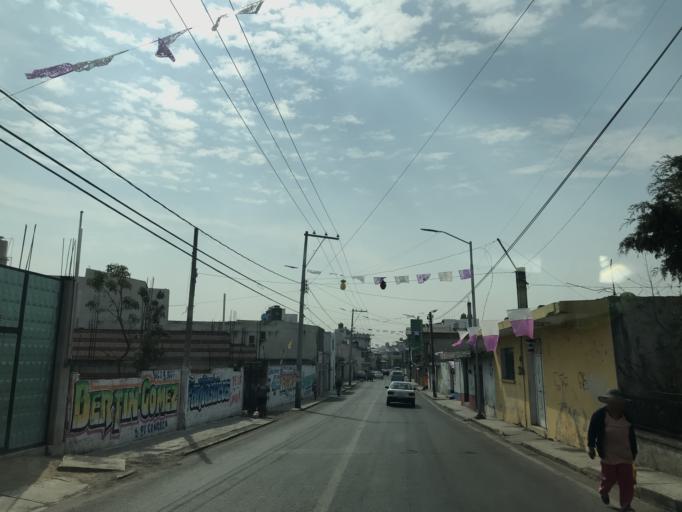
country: MX
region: Tlaxcala
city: Tenancingo
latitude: 19.1475
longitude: -98.2005
